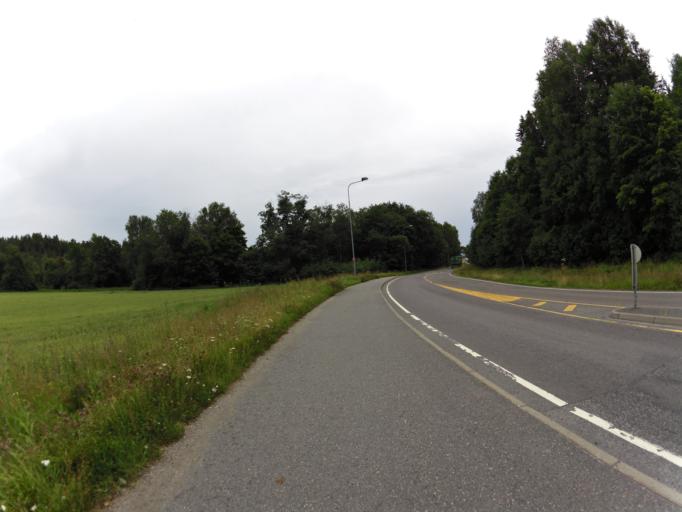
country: NO
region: Ostfold
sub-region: Moss
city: Moss
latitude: 59.4769
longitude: 10.6946
